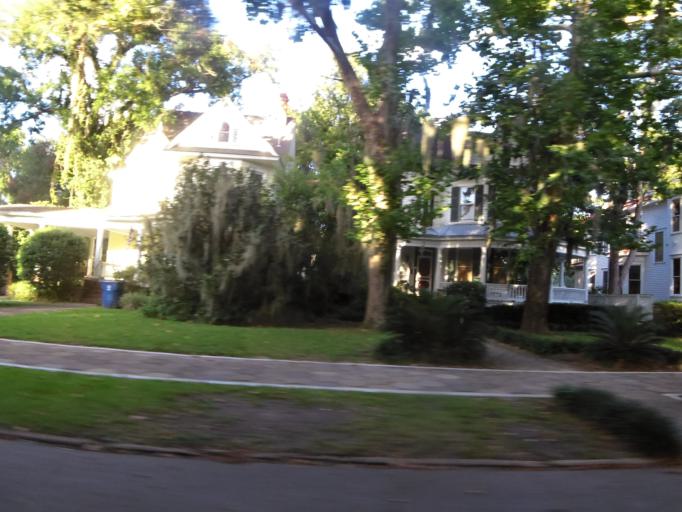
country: US
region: Georgia
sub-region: Glynn County
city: Brunswick
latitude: 31.1432
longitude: -81.4910
